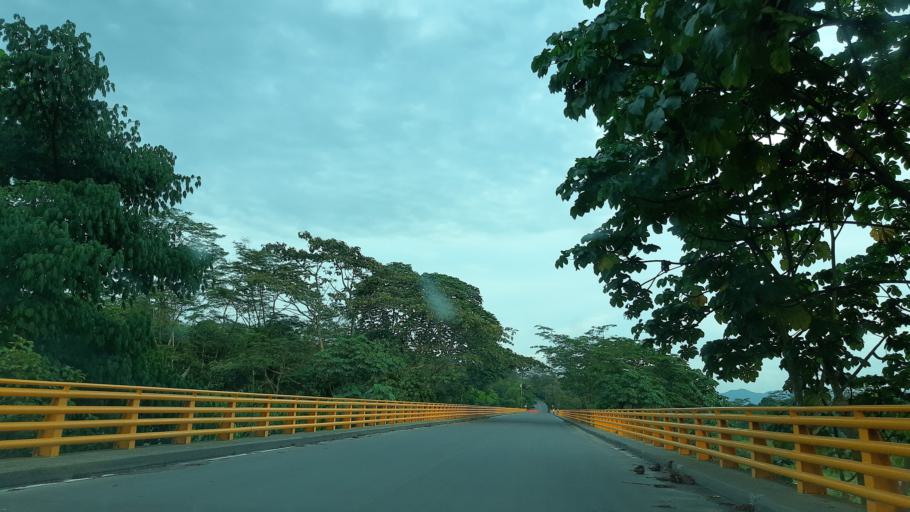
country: CO
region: Casanare
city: Sabanalarga
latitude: 4.8216
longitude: -73.0749
